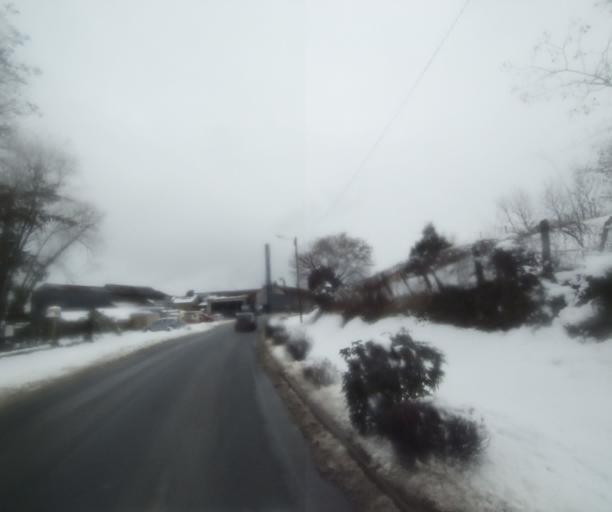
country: FR
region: Champagne-Ardenne
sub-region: Departement de la Haute-Marne
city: Wassy
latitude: 48.4872
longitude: 4.9683
